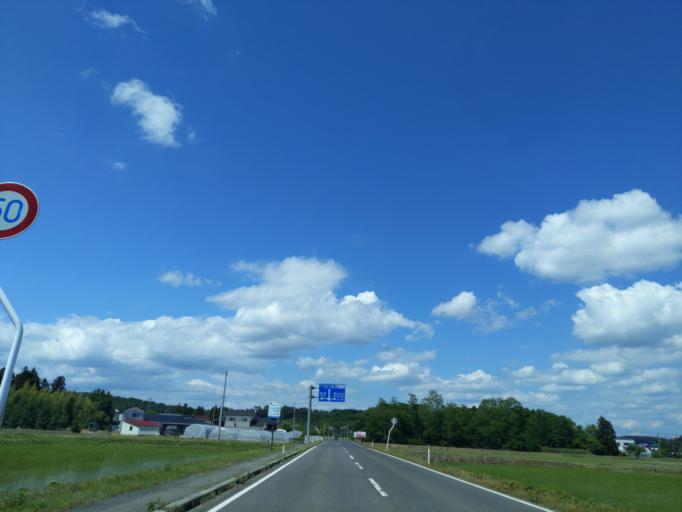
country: JP
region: Fukushima
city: Koriyama
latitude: 37.3872
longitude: 140.3008
